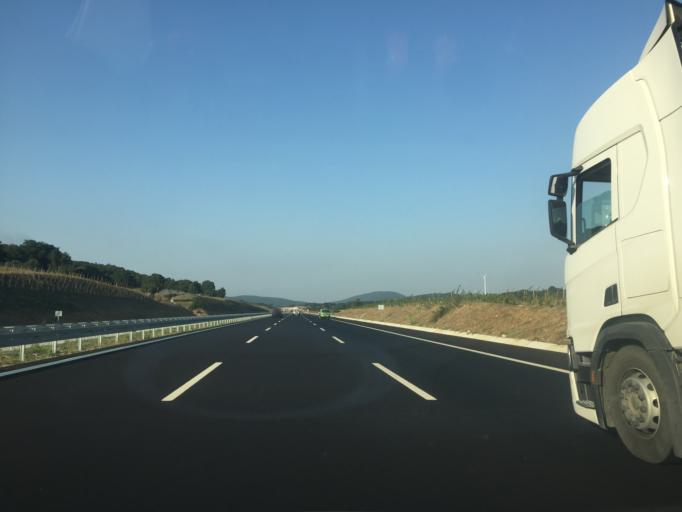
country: TR
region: Balikesir
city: Ertugrul
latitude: 39.4871
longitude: 27.6564
